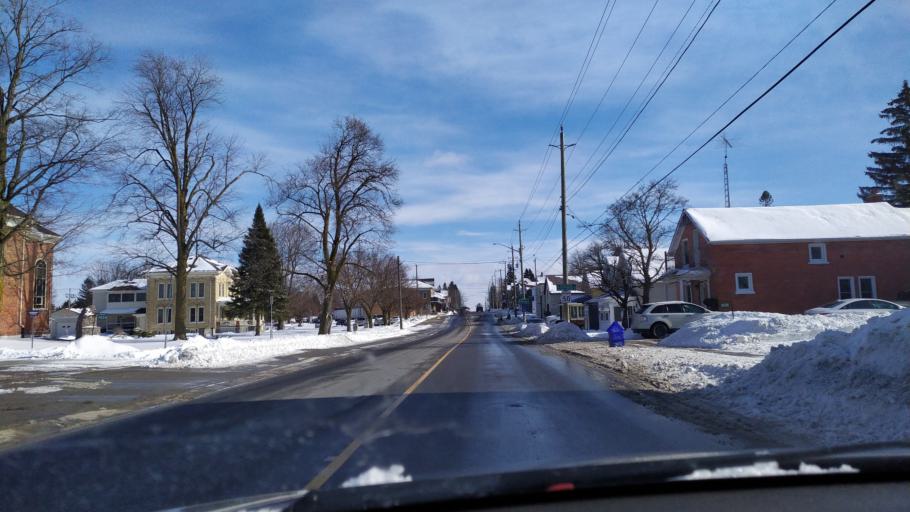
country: CA
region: Ontario
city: Waterloo
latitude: 43.5233
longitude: -80.6542
